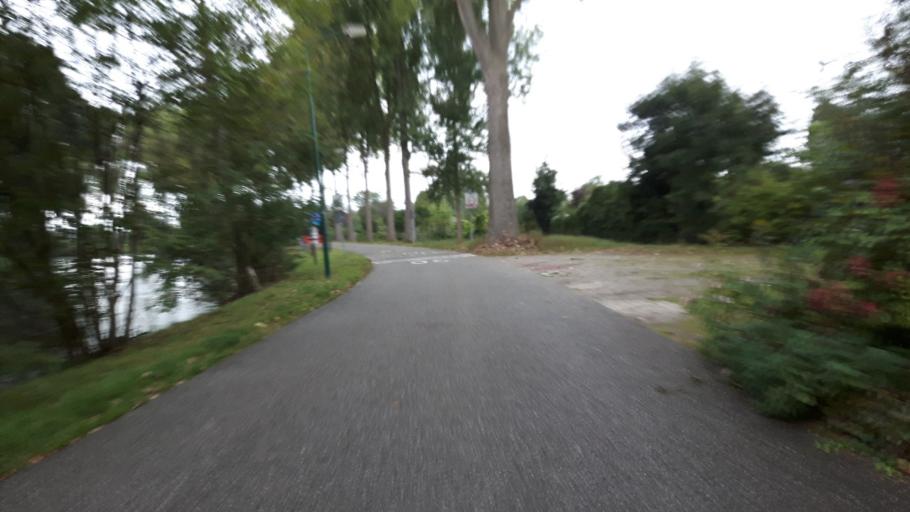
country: NL
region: Utrecht
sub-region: Stichtse Vecht
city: Maarssen
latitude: 52.1299
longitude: 5.0690
